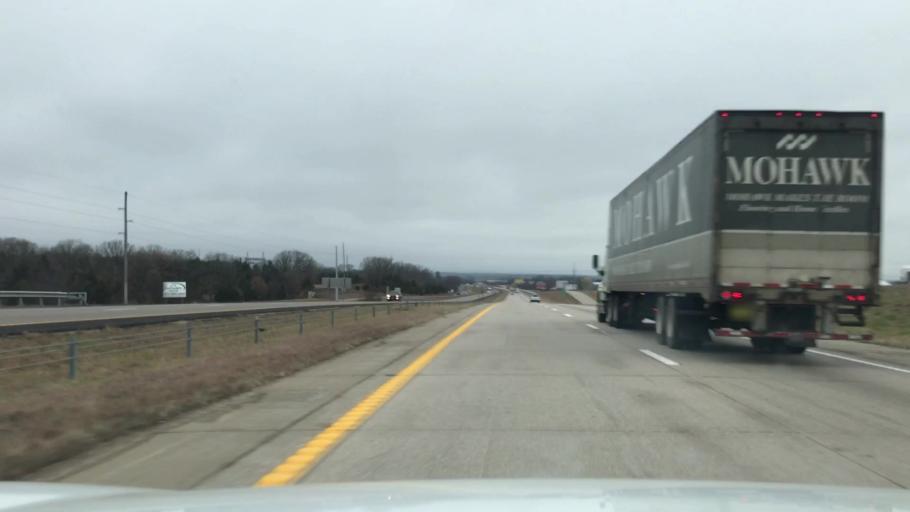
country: US
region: Missouri
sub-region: Franklin County
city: Sullivan
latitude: 38.1840
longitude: -91.2002
